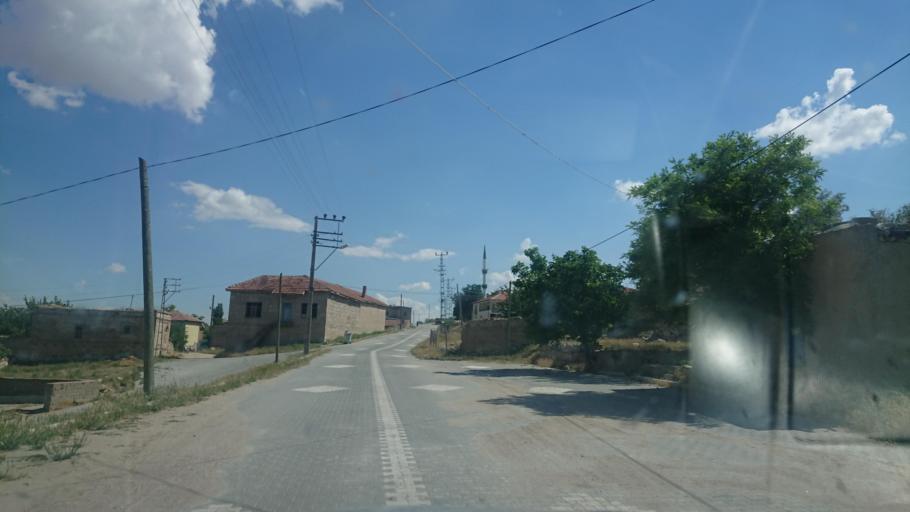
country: TR
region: Aksaray
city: Agacoren
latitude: 38.7710
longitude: 33.7852
